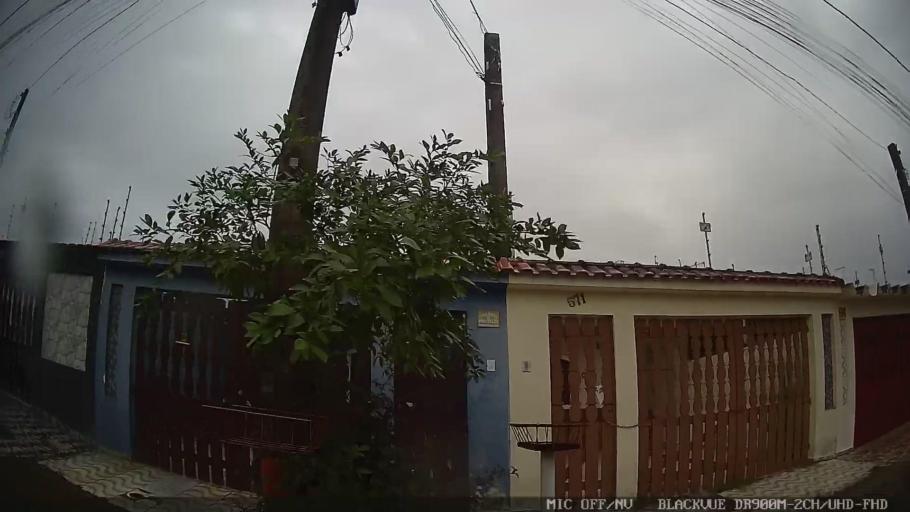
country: BR
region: Sao Paulo
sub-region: Itanhaem
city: Itanhaem
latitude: -24.1691
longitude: -46.7648
